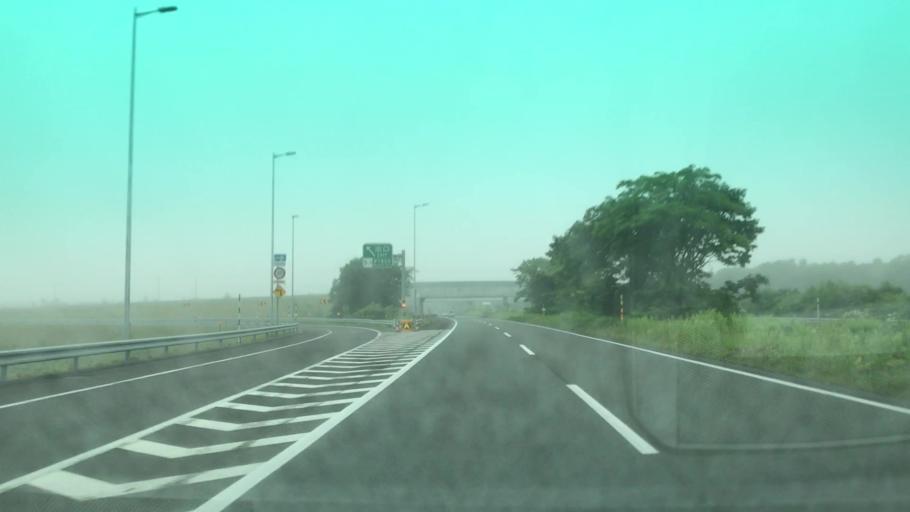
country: JP
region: Hokkaido
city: Chitose
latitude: 42.7784
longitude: 141.6276
